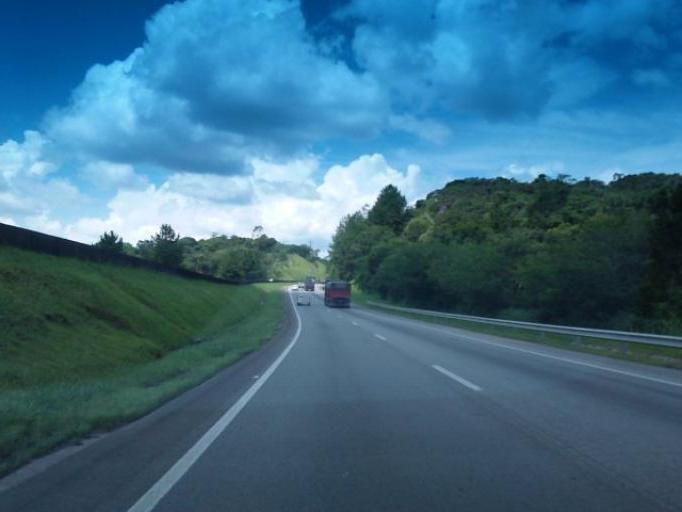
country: BR
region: Sao Paulo
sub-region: Juquitiba
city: Juquitiba
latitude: -23.9619
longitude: -47.1217
